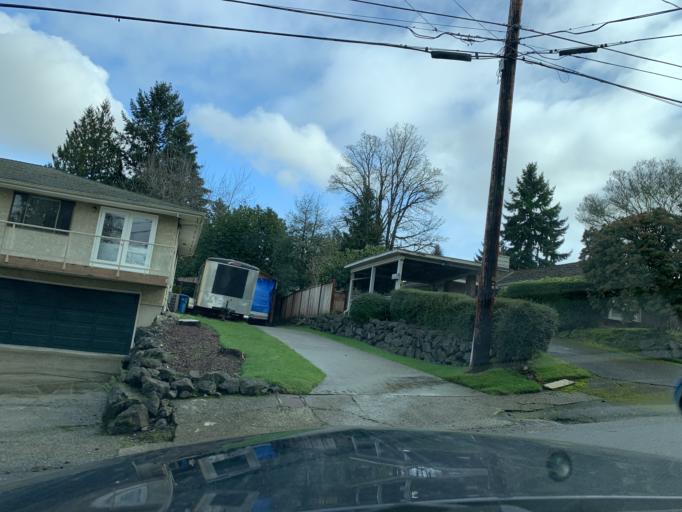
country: US
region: Washington
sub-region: King County
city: Mercer Island
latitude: 47.5875
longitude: -122.2452
